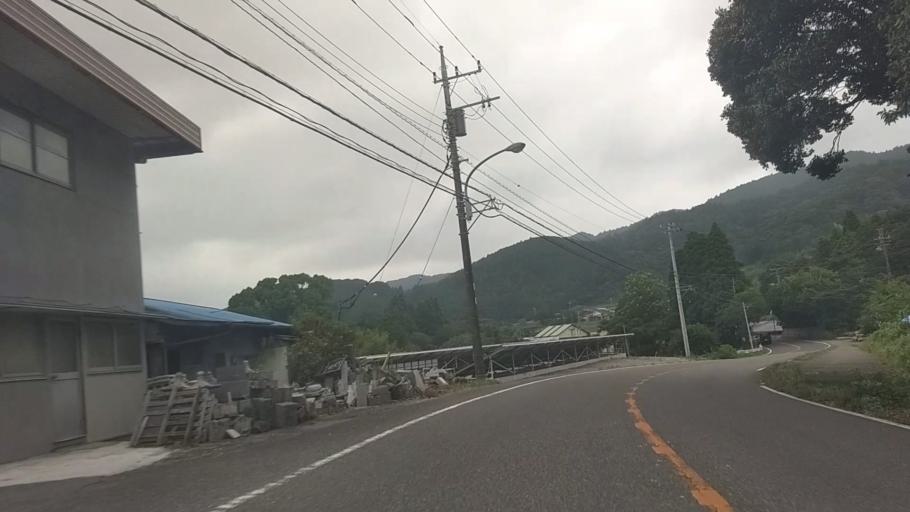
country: JP
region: Chiba
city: Kawaguchi
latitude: 35.1409
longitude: 139.9731
